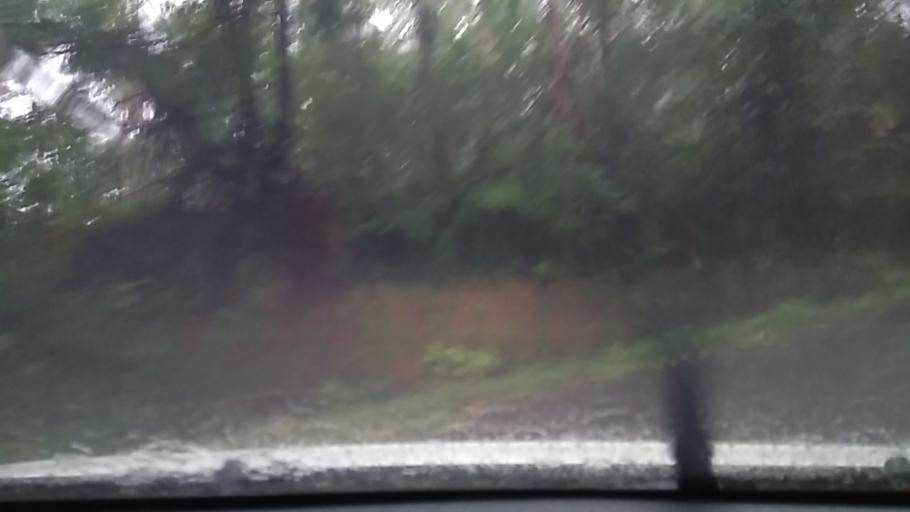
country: ID
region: Bali
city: Banjar Ambengan
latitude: -8.2137
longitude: 115.1723
